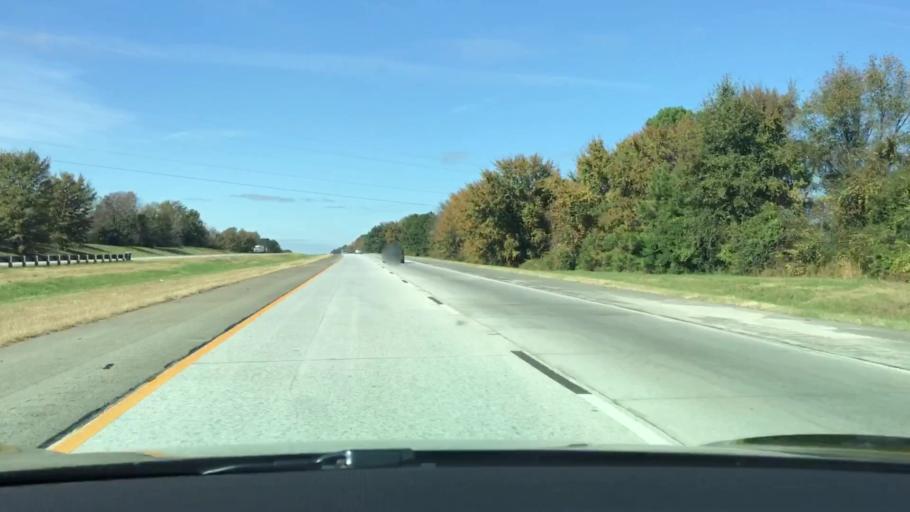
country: US
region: Georgia
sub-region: Putnam County
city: Jefferson
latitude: 33.5403
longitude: -83.3156
